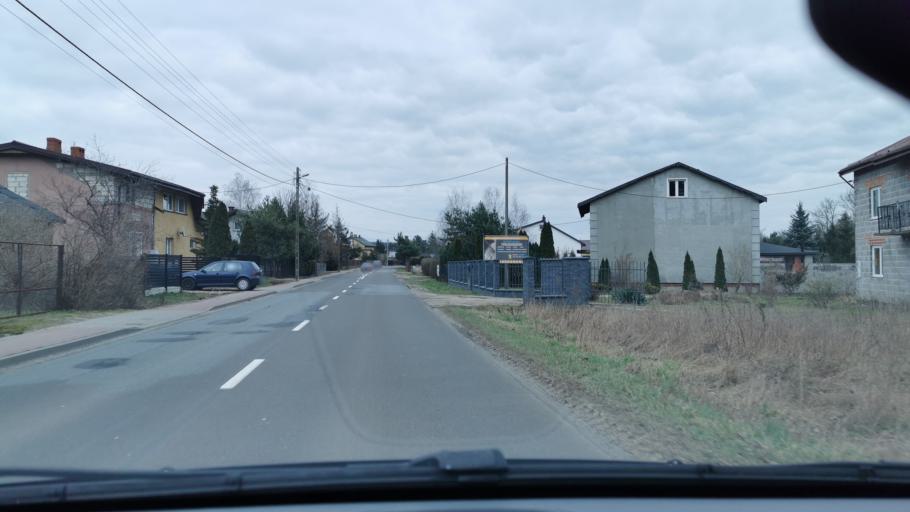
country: PL
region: Masovian Voivodeship
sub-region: Powiat zyrardowski
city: Radziejowice
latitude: 52.0090
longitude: 20.5438
